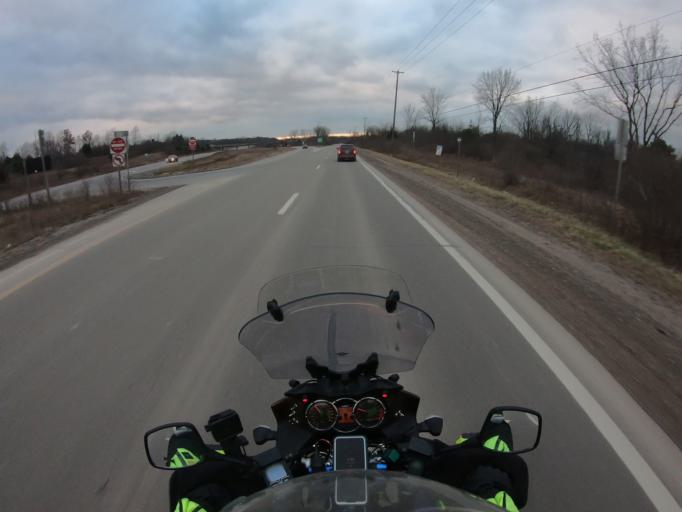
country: US
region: Michigan
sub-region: Genesee County
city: Grand Blanc
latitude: 42.8670
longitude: -83.5872
